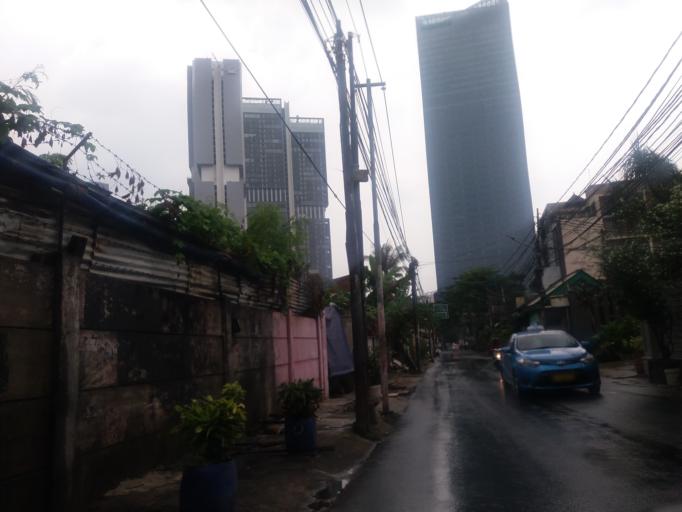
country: ID
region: Jakarta Raya
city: Jakarta
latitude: -6.2214
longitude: 106.8226
